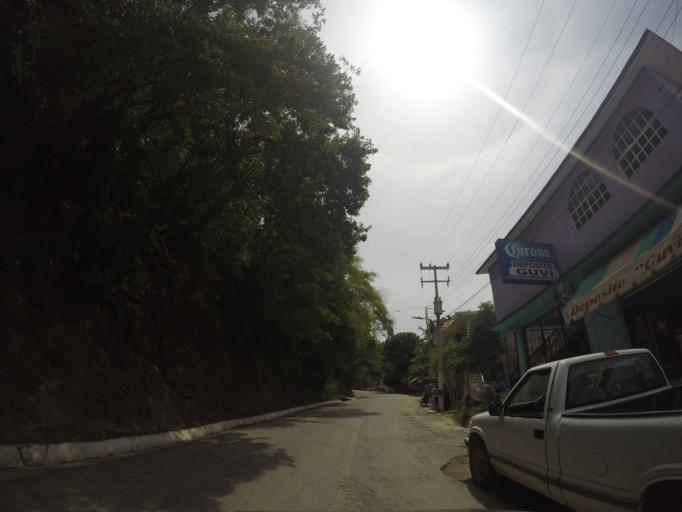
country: MX
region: Oaxaca
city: San Pedro Pochutla
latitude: 15.6680
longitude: -96.4948
